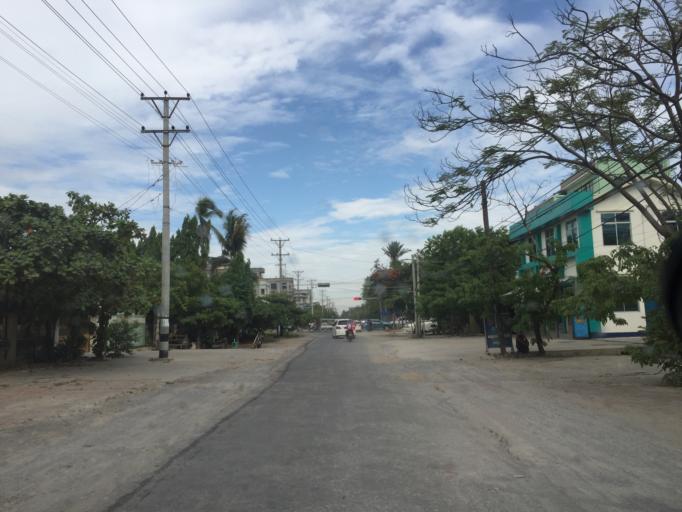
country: MM
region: Mandalay
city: Mandalay
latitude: 21.9726
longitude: 96.1069
